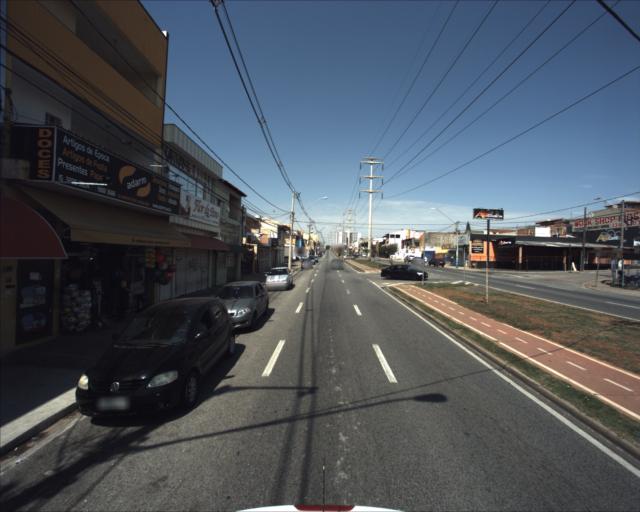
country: BR
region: Sao Paulo
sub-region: Sorocaba
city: Sorocaba
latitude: -23.4508
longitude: -47.4882
